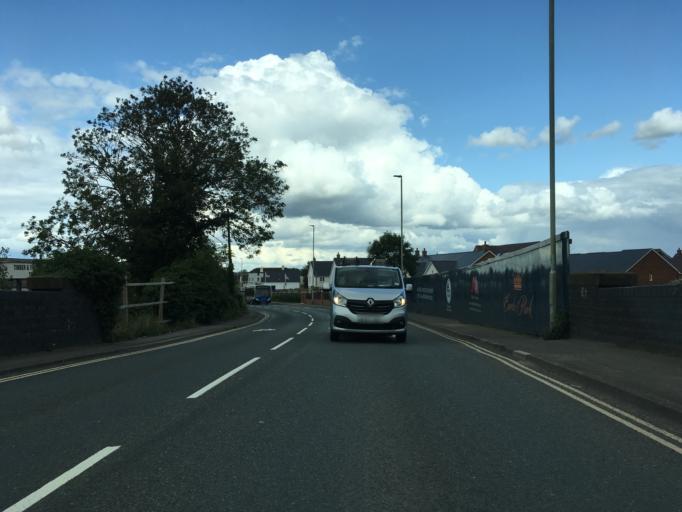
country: GB
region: England
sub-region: Gloucestershire
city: Gloucester
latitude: 51.8474
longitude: -2.2607
